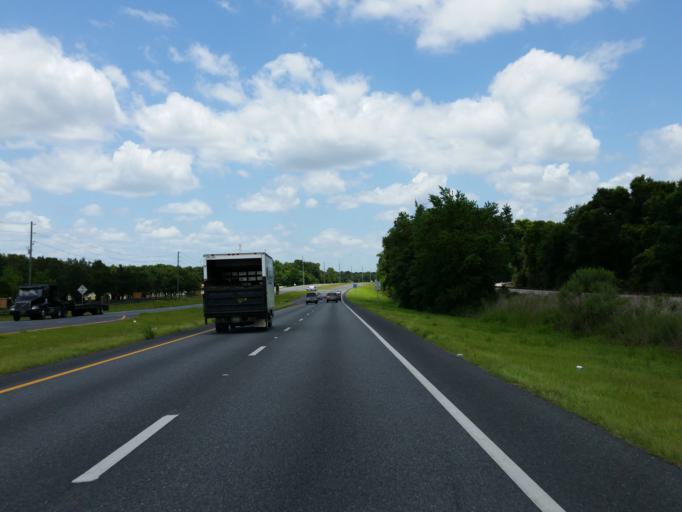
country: US
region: Florida
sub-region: Sumter County
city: The Villages
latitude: 28.9611
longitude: -82.0406
